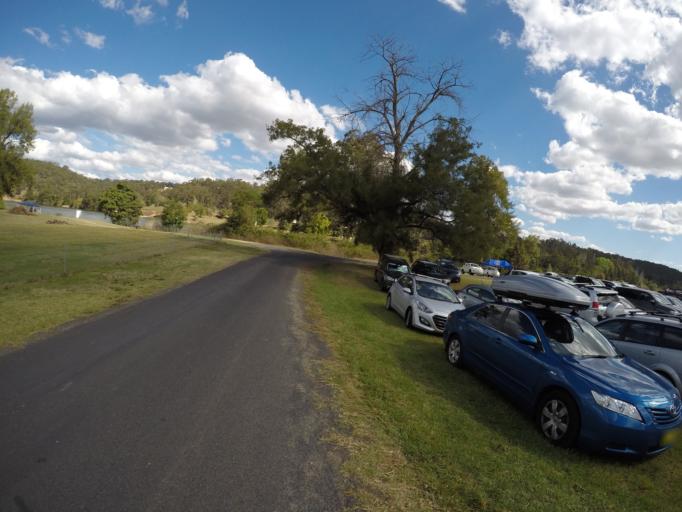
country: AU
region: New South Wales
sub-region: Hawkesbury
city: Pitt Town
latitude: -33.4721
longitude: 150.8907
